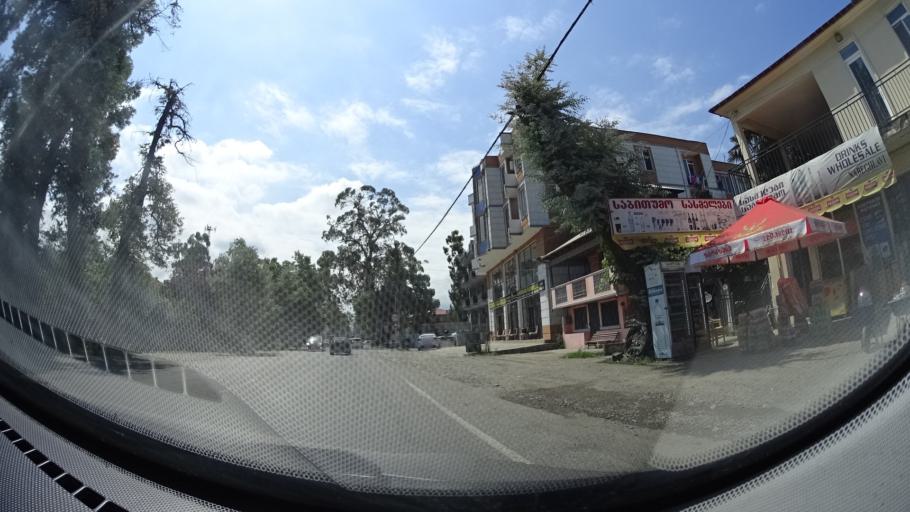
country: GE
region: Ajaria
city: Batumi
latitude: 41.6165
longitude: 41.6199
